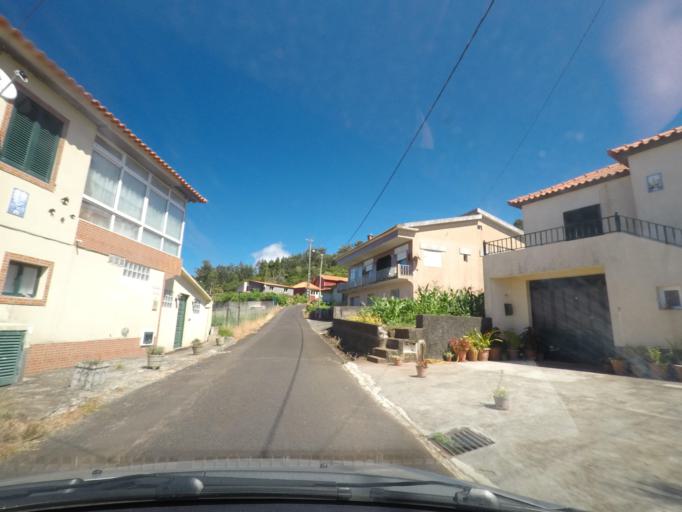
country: PT
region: Madeira
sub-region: Porto Moniz
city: Porto Moniz
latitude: 32.8418
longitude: -17.2062
